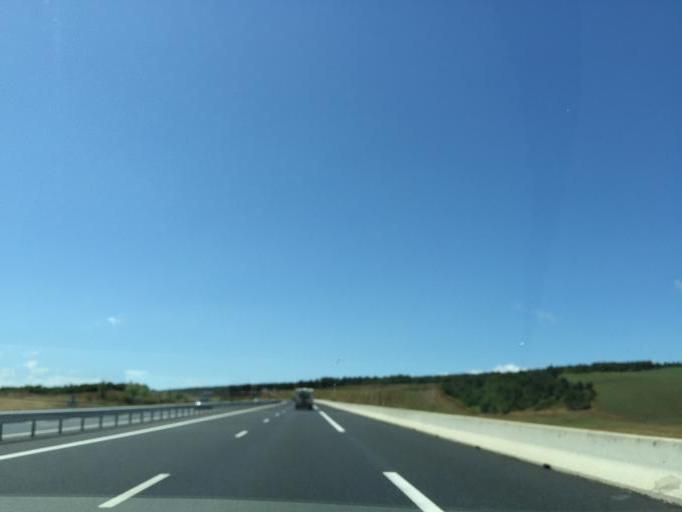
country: FR
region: Midi-Pyrenees
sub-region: Departement de l'Aveyron
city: Millau
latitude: 44.1820
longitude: 3.0419
